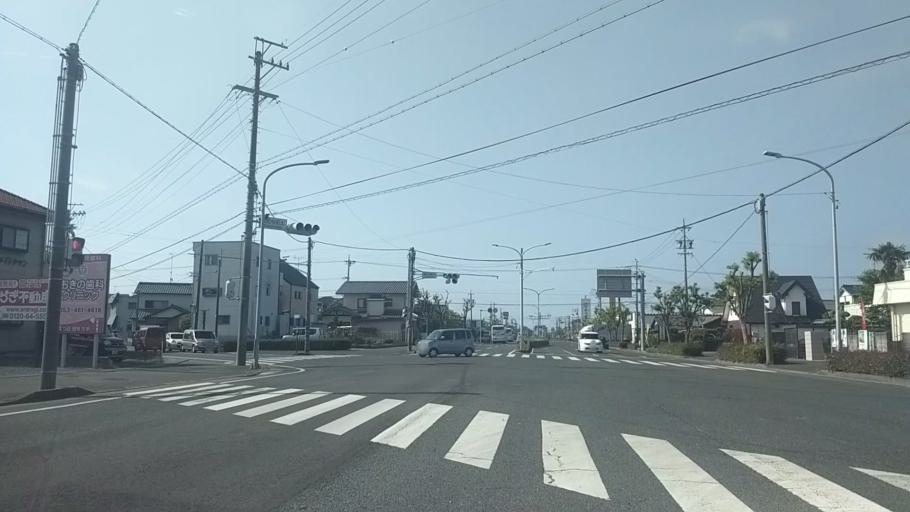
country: JP
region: Shizuoka
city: Hamamatsu
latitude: 34.7009
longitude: 137.7571
